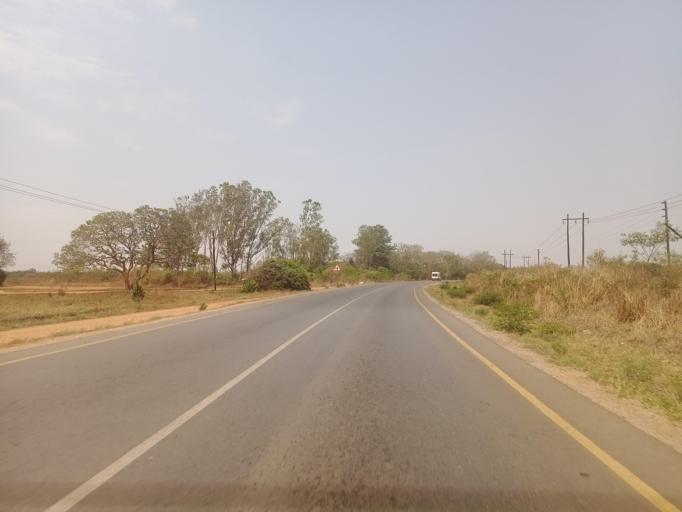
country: ZM
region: Lusaka
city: Lusaka
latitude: -15.2769
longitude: 28.4033
